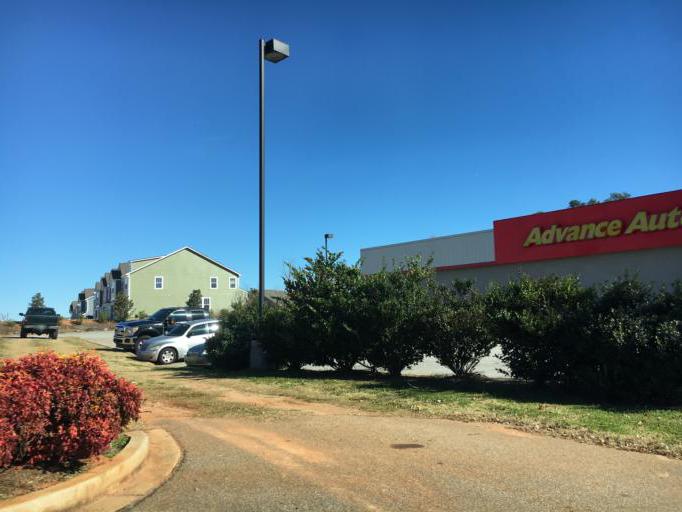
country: US
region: South Carolina
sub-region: Spartanburg County
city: Wellford
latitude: 34.8886
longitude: -82.0704
